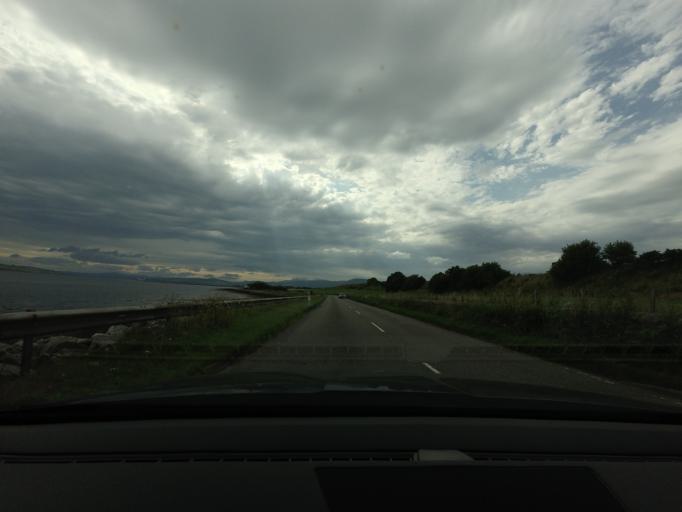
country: GB
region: Scotland
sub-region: Highland
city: Invergordon
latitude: 57.6927
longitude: -4.2049
